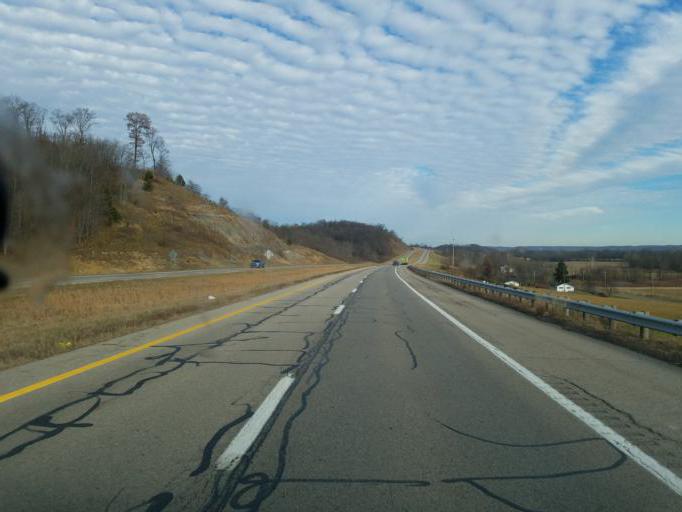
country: US
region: Ohio
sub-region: Muskingum County
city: Frazeysburg
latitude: 40.1501
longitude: -82.0711
